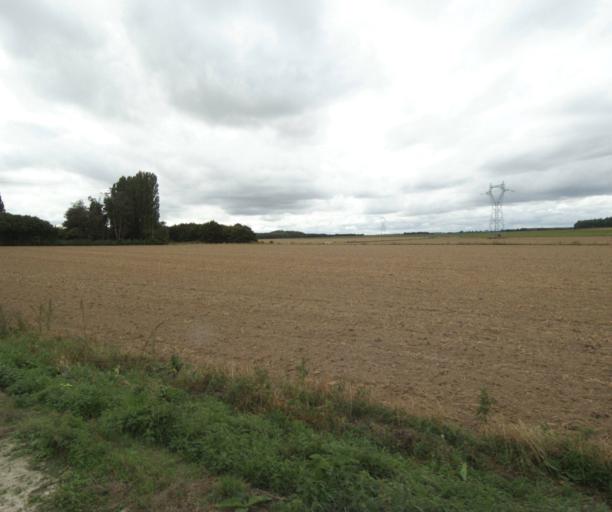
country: FR
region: Nord-Pas-de-Calais
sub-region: Departement du Nord
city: Sainghin-en-Melantois
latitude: 50.5734
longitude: 3.1728
